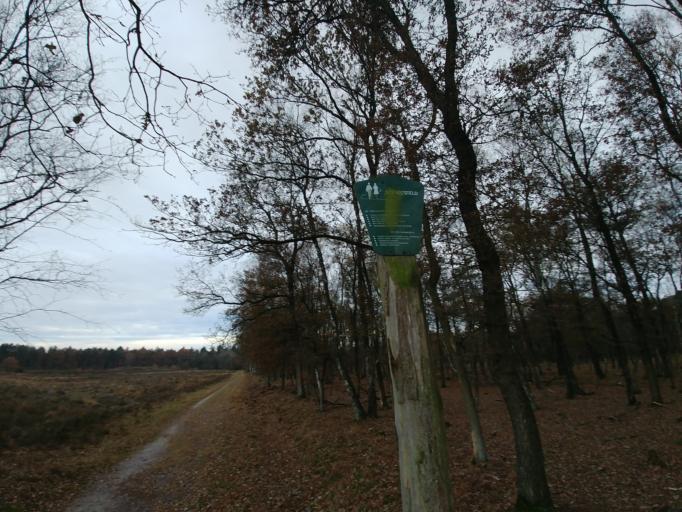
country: NL
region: Utrecht
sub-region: Gemeente Utrechtse Heuvelrug
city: Overberg
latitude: 52.0226
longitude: 5.5090
